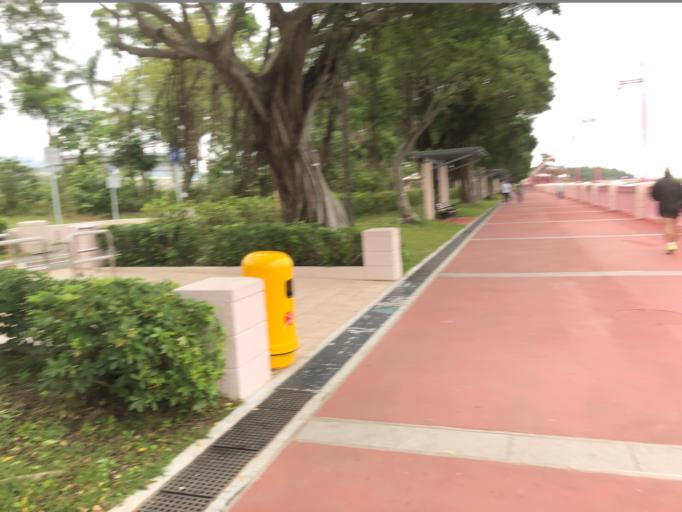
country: HK
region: Tai Po
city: Tai Po
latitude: 22.4527
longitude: 114.1832
